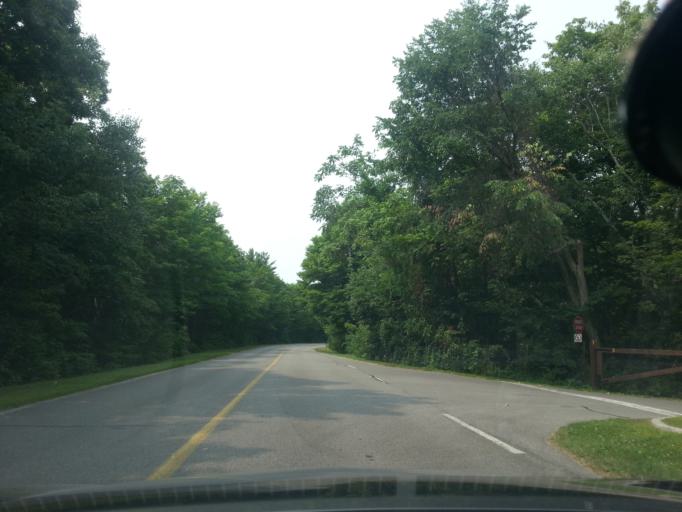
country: CA
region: Quebec
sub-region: Outaouais
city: Gatineau
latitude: 45.4665
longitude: -75.8081
